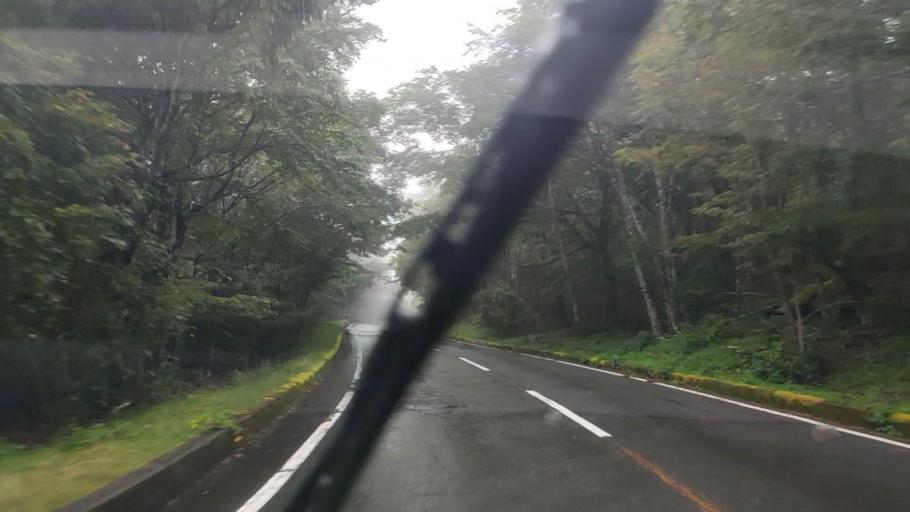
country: JP
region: Shizuoka
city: Fuji
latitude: 35.3126
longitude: 138.7408
